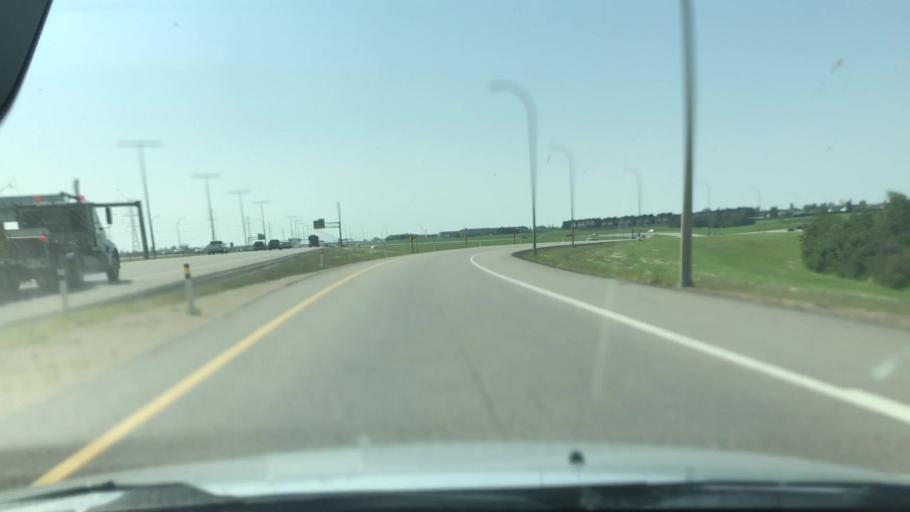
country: CA
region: Alberta
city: St. Albert
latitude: 53.5157
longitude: -113.6601
